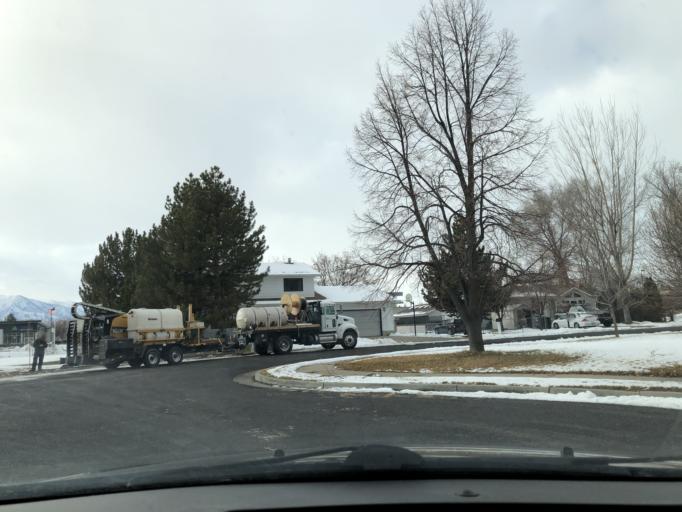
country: US
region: Utah
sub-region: Cache County
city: River Heights
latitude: 41.7185
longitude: -111.8331
